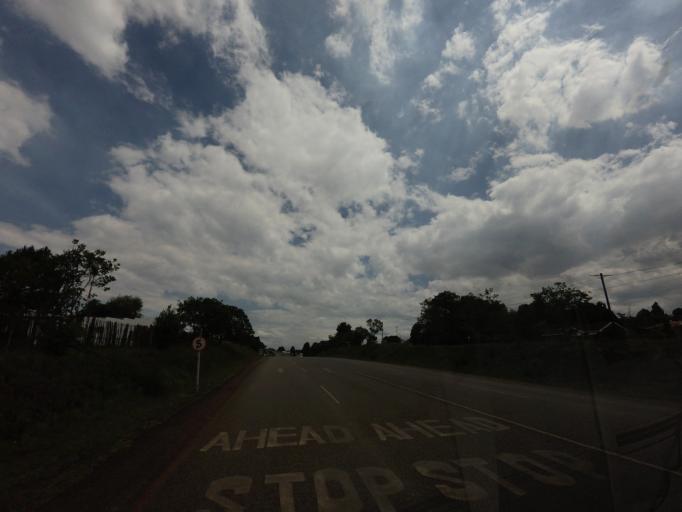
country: ZA
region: Mpumalanga
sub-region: Ehlanzeni District
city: Graksop
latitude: -24.9294
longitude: 30.8378
